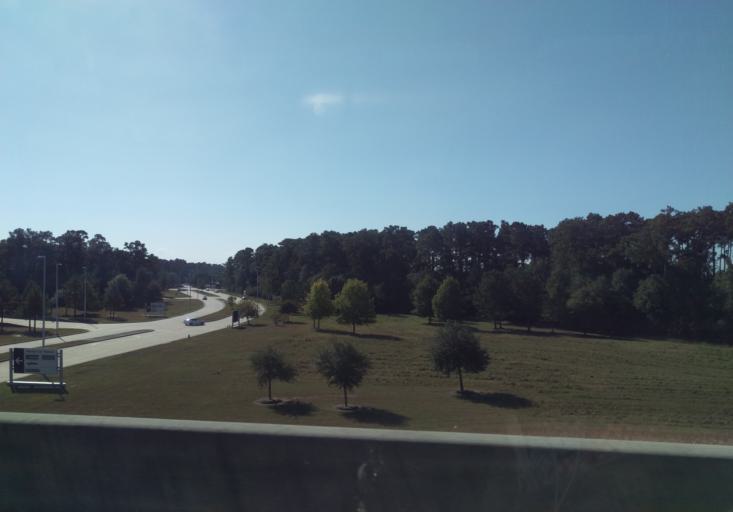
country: US
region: Texas
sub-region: Harris County
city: Aldine
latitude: 29.9696
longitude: -95.3360
